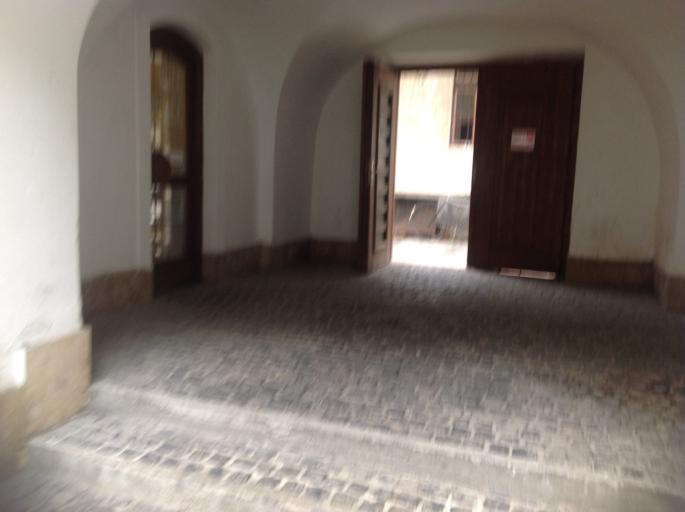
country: HU
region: Gyor-Moson-Sopron
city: Gyor
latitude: 47.6875
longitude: 17.6337
